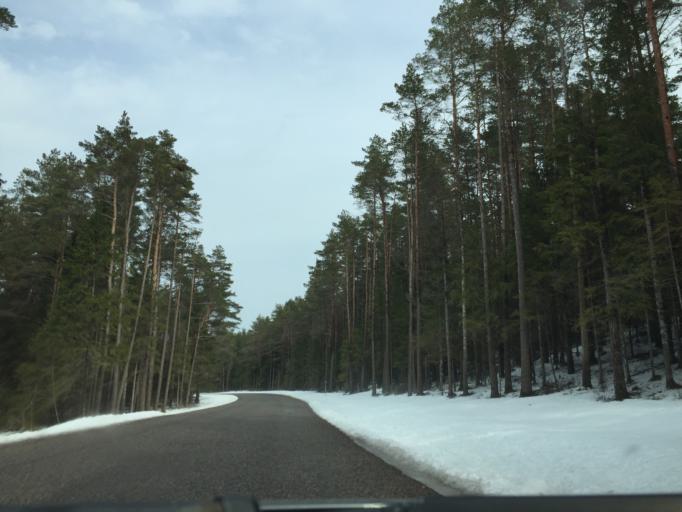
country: EE
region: Saare
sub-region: Kuressaare linn
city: Kuressaare
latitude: 58.4006
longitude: 22.1721
